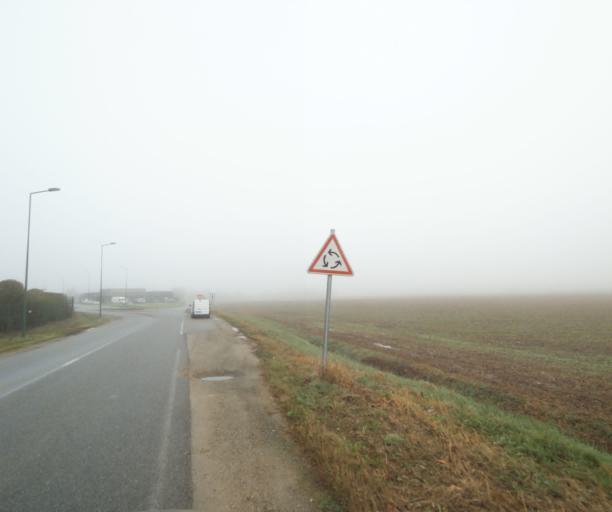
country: FR
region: Midi-Pyrenees
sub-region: Departement de la Haute-Garonne
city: Villemur-sur-Tarn
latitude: 43.8420
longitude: 1.4994
